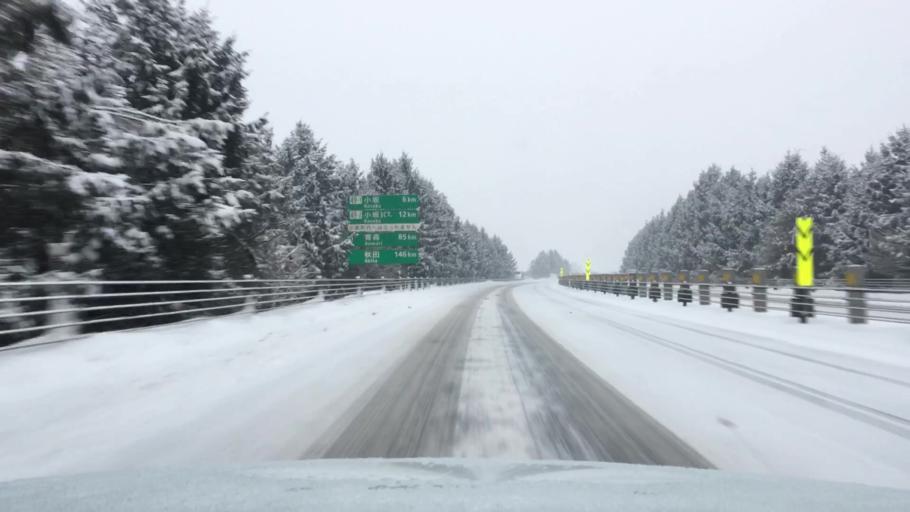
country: JP
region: Akita
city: Hanawa
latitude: 40.2701
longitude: 140.7631
